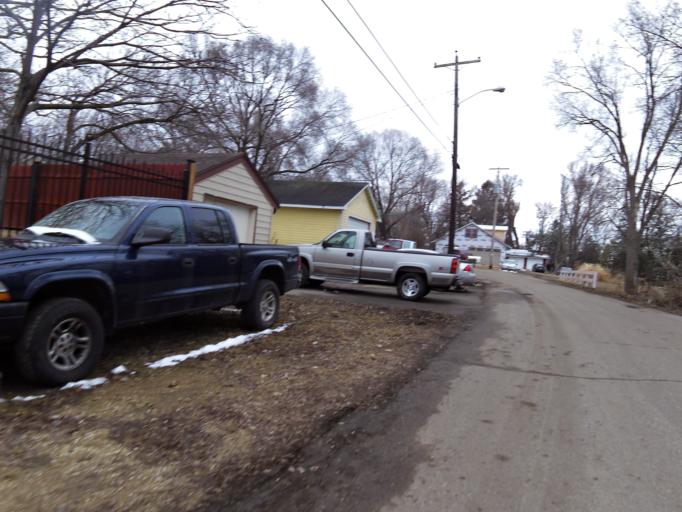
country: US
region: Wisconsin
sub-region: Saint Croix County
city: North Hudson
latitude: 44.9856
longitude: -92.7581
